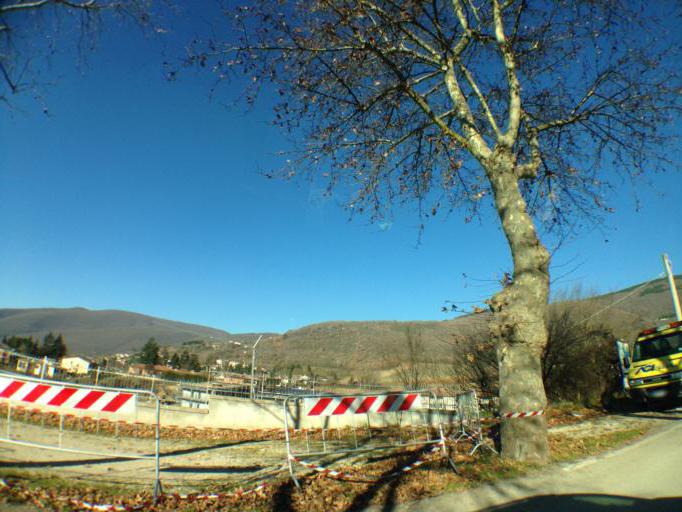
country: IT
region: Umbria
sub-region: Provincia di Perugia
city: Norcia
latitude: 42.7979
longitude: 13.0941
